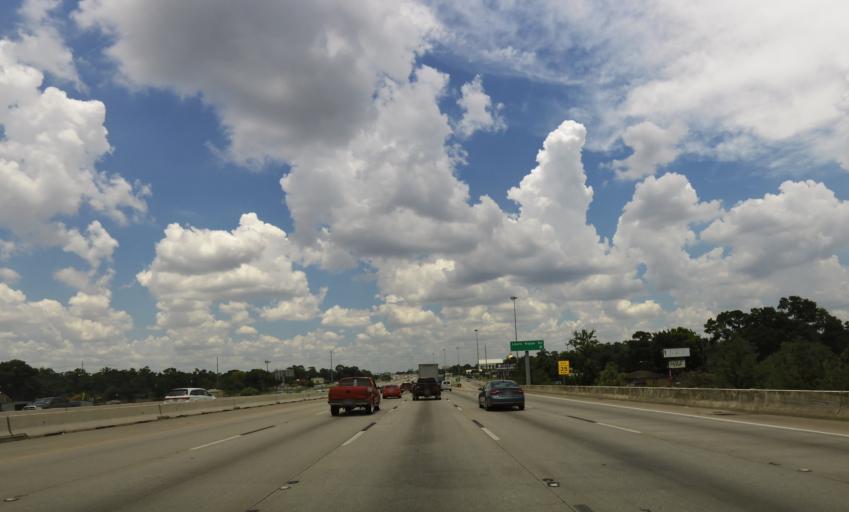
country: US
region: Texas
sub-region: Harris County
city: Houston
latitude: 29.8312
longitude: -95.3353
